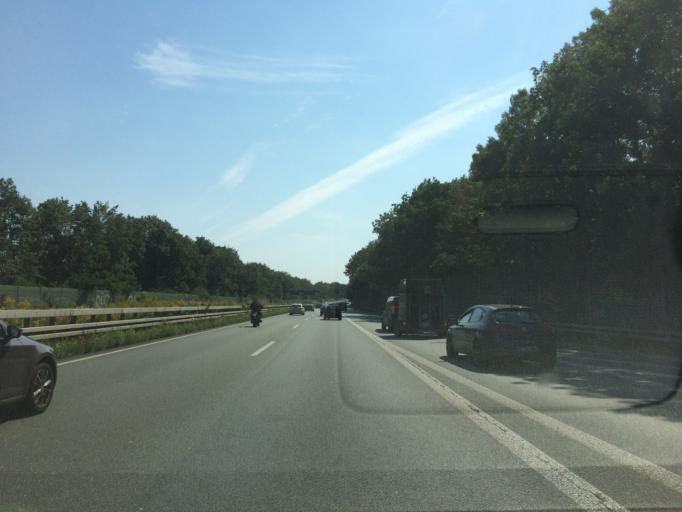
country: DE
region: North Rhine-Westphalia
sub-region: Regierungsbezirk Munster
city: Recklinghausen
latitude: 51.6068
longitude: 7.1781
